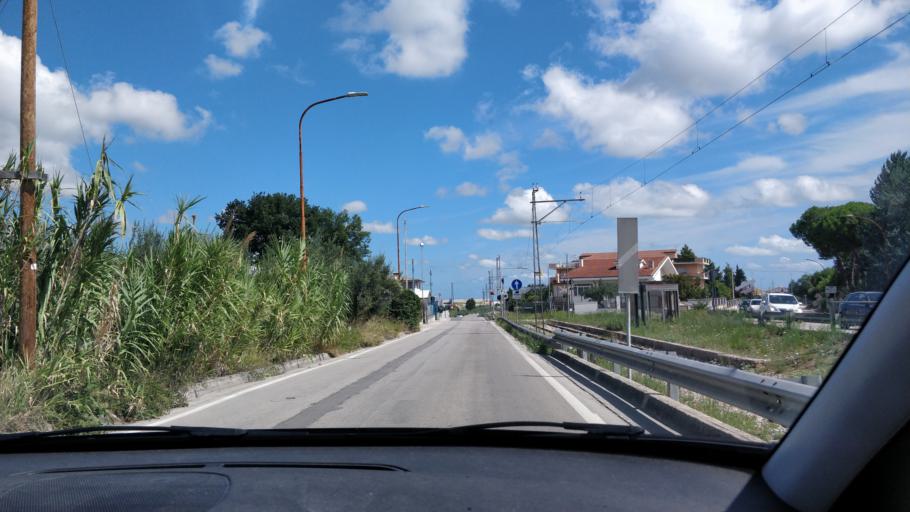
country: IT
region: Abruzzo
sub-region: Provincia di Chieti
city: Lanciano
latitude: 42.2339
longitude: 14.4059
